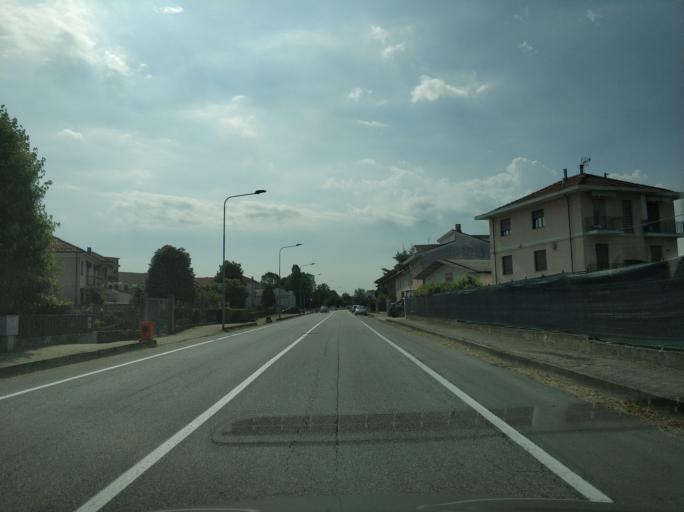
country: IT
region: Piedmont
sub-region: Provincia di Torino
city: Poirino
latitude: 44.9140
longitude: 7.8469
